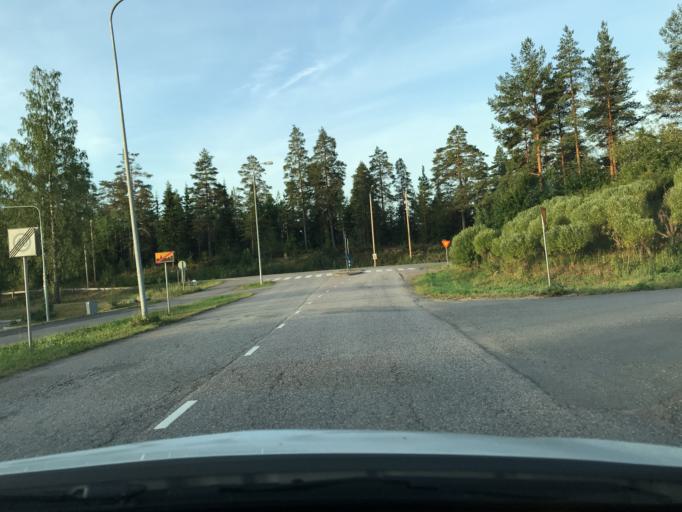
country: FI
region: Uusimaa
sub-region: Helsinki
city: Vihti
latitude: 60.3992
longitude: 24.4785
